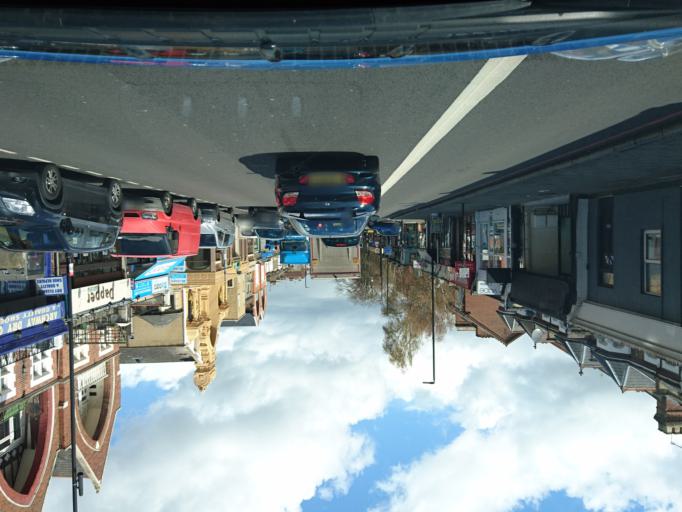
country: GB
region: England
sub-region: Greater London
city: Crouch End
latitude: 51.5729
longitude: -0.1406
